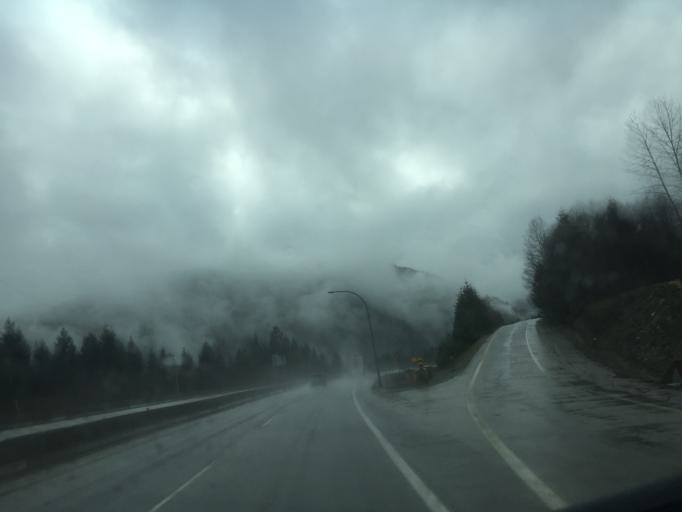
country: CA
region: British Columbia
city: Hope
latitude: 49.4959
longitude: -121.2067
